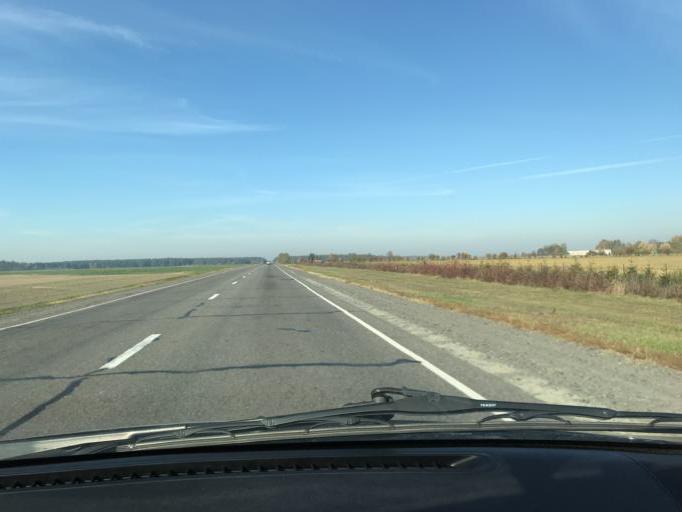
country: BY
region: Brest
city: Davyd-Haradok
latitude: 52.2504
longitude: 27.0661
